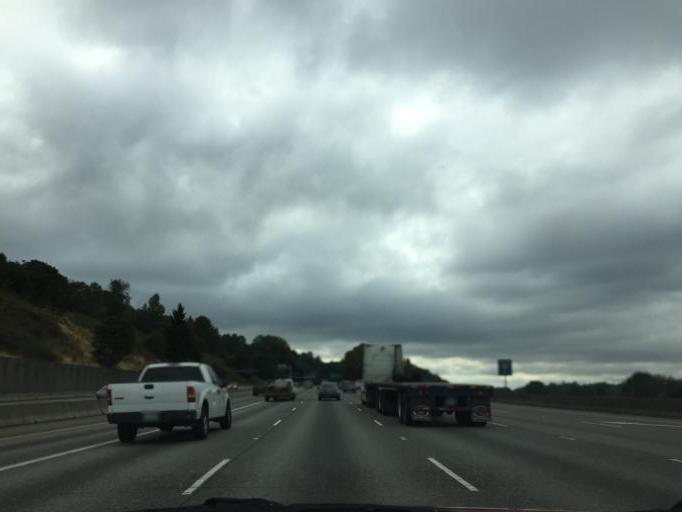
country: US
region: Washington
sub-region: King County
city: Tukwila
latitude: 47.4956
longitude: -122.2698
